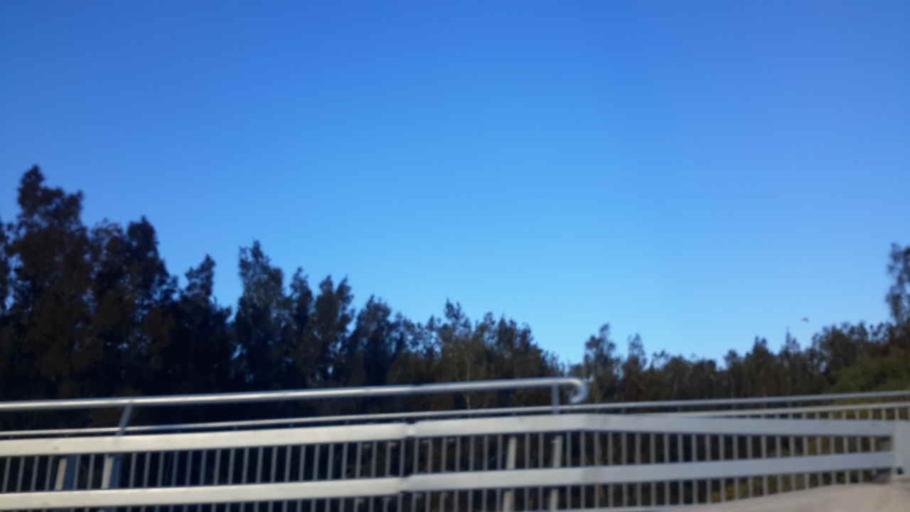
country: AU
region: New South Wales
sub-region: Camden
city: Narellan
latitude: -34.0286
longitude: 150.7273
